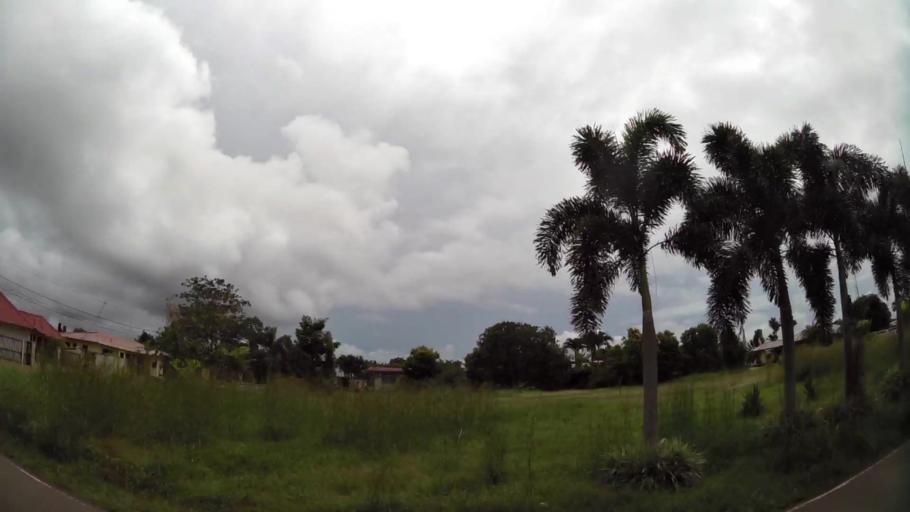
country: PA
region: Chiriqui
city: David
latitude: 8.4211
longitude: -82.4524
